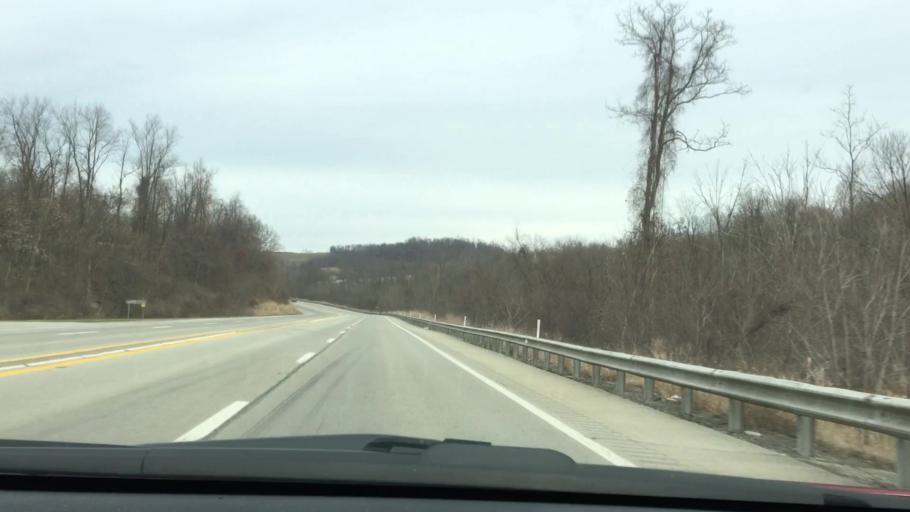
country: US
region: Pennsylvania
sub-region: Fayette County
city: Perryopolis
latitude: 40.0296
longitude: -79.7709
